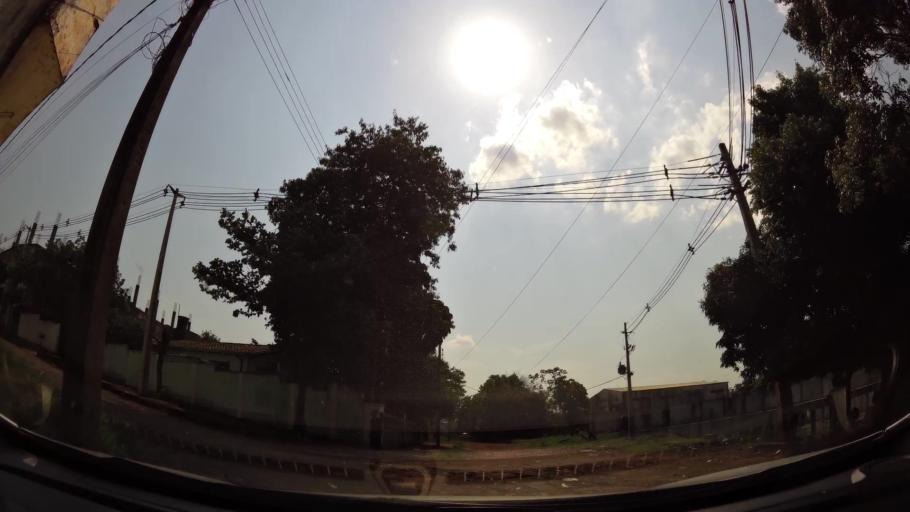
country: PY
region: Alto Parana
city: Ciudad del Este
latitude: -25.5051
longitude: -54.6223
